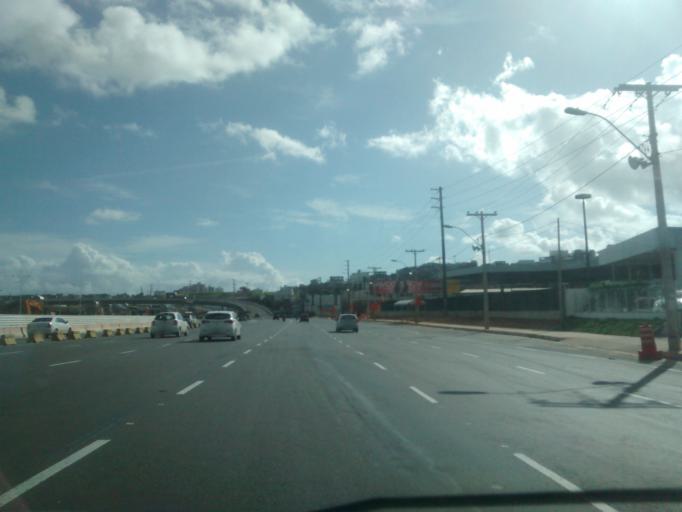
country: BR
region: Bahia
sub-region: Salvador
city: Salvador
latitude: -12.9755
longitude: -38.4564
